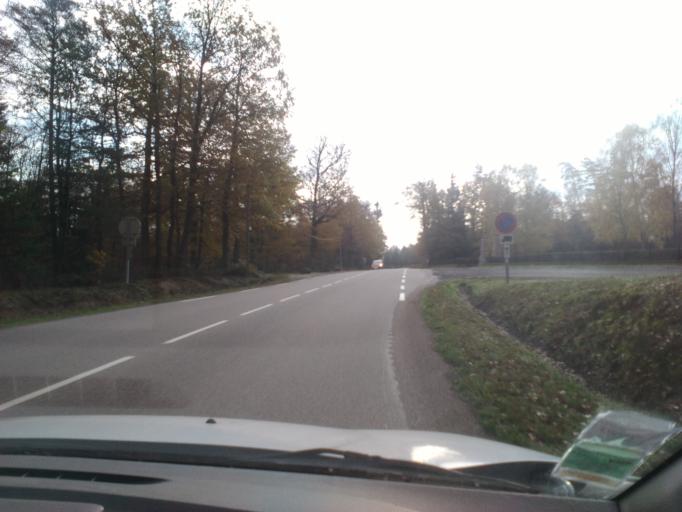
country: FR
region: Lorraine
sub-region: Departement de Meurthe-et-Moselle
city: Baccarat
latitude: 48.3707
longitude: 6.7736
